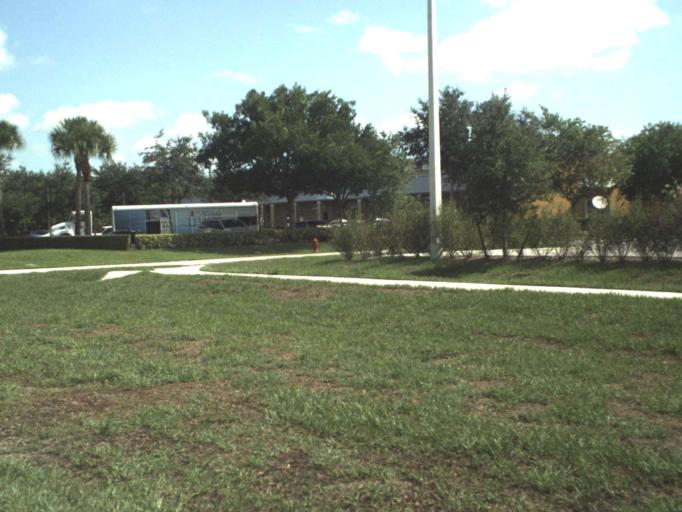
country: US
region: Florida
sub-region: Saint Lucie County
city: Port Saint Lucie
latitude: 27.2273
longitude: -80.3729
